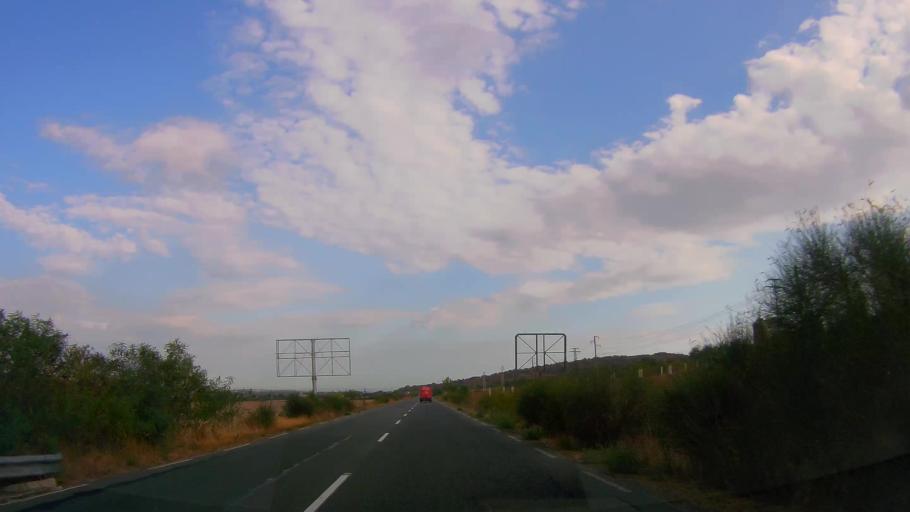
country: BG
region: Burgas
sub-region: Obshtina Sozopol
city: Sozopol
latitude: 42.3744
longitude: 27.6826
